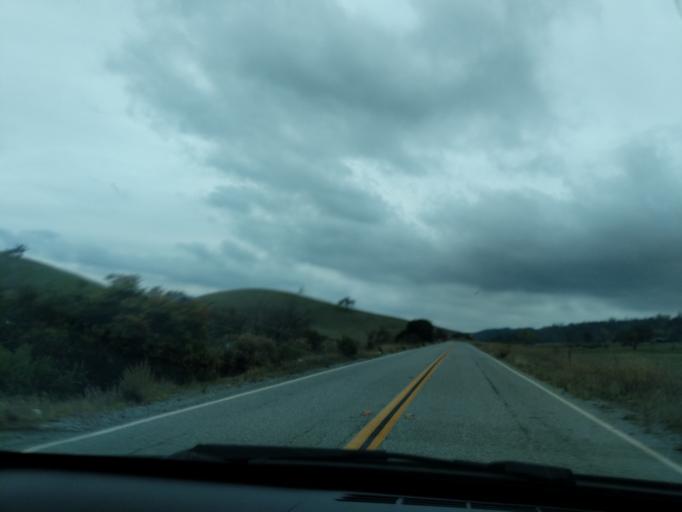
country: US
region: California
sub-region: Monterey County
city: Soledad
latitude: 36.5751
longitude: -121.1857
